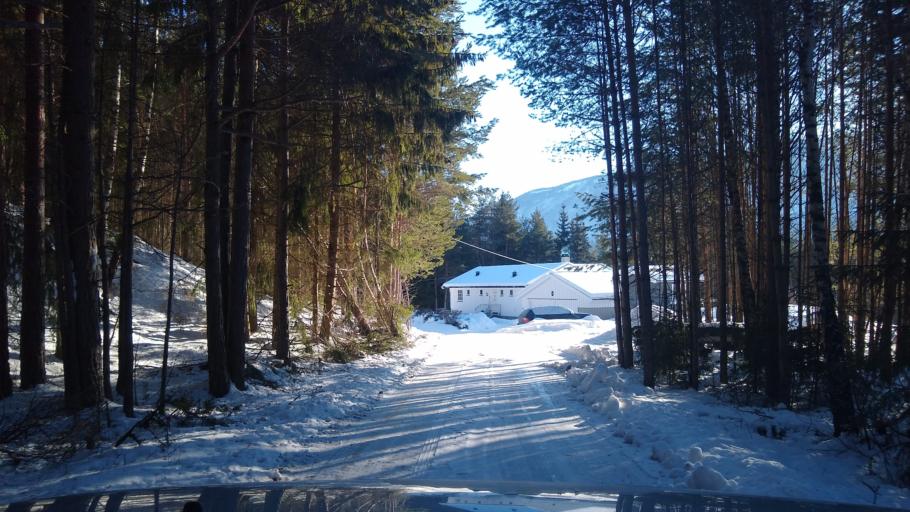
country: NO
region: Oppland
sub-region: Ringebu
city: Ringebu
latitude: 61.5511
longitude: 10.0686
